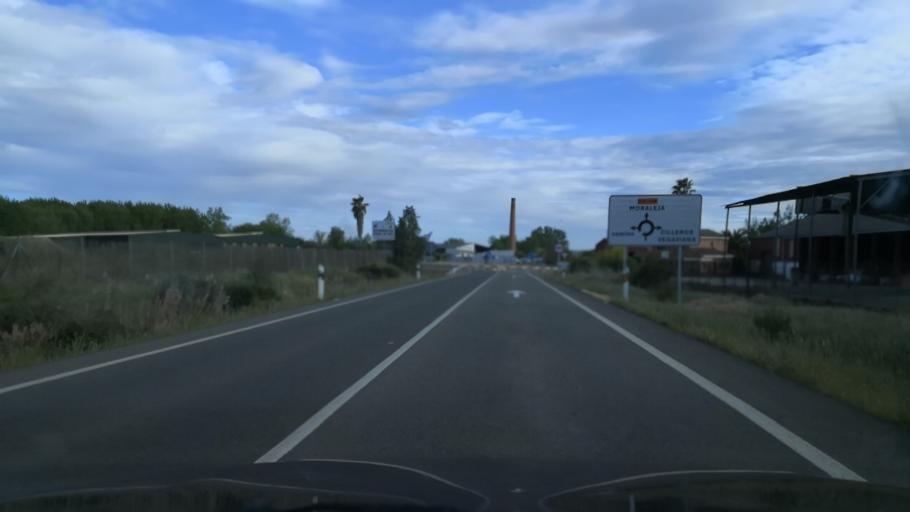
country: ES
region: Extremadura
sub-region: Provincia de Caceres
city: Moraleja
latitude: 40.0789
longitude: -6.6689
